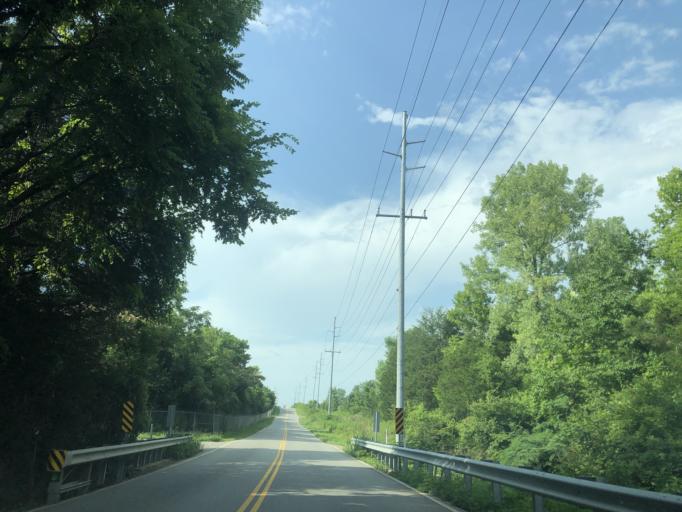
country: US
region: Tennessee
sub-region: Davidson County
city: Oak Hill
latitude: 36.1180
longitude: -86.6597
